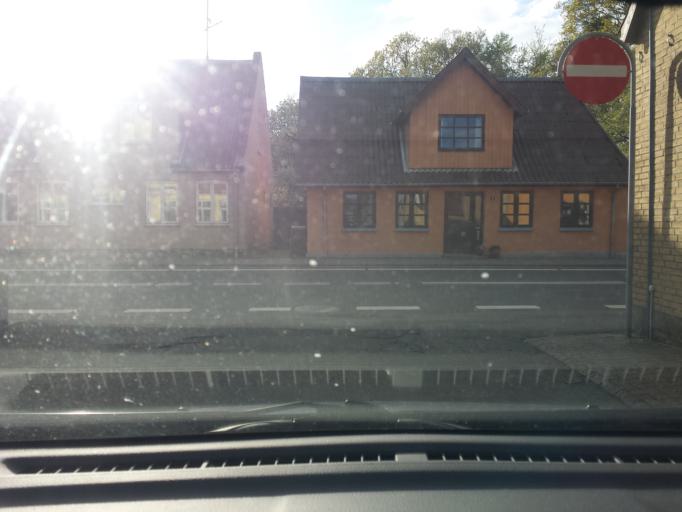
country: DK
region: South Denmark
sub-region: Langeland Kommune
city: Rudkobing
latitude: 54.8638
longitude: 10.7295
